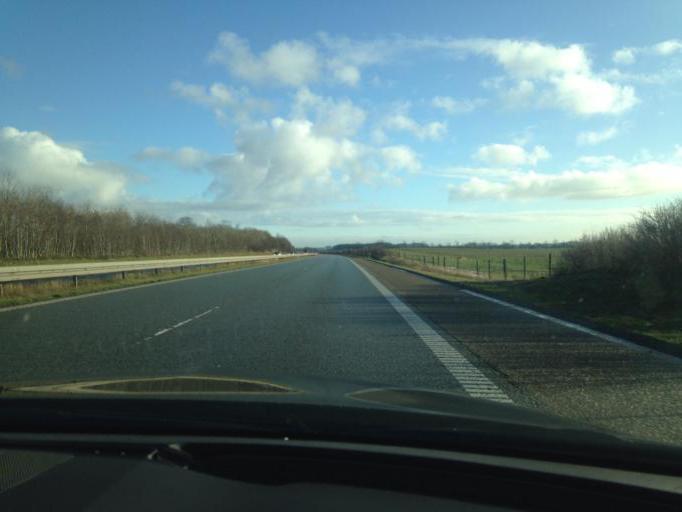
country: DK
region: South Denmark
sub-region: Vejen Kommune
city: Holsted
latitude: 55.5128
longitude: 8.9553
